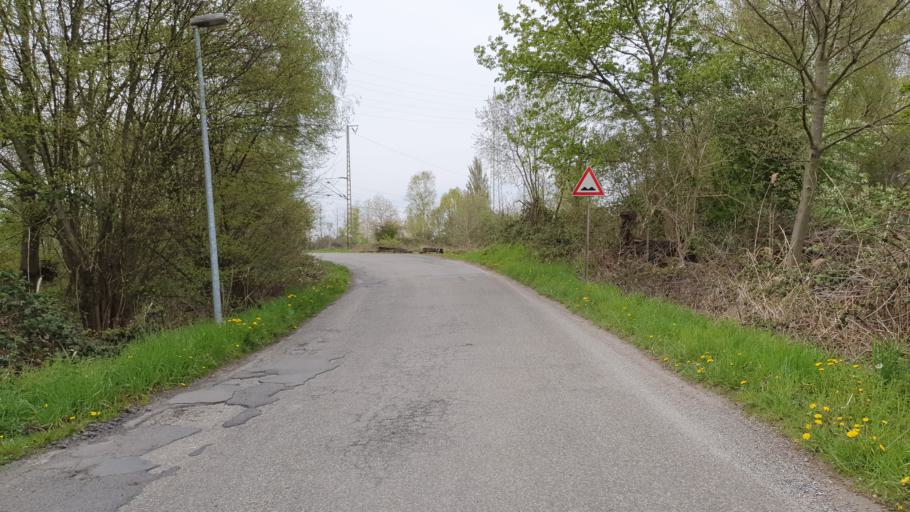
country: DE
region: North Rhine-Westphalia
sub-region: Regierungsbezirk Dusseldorf
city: Oberhausen
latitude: 51.5041
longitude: 6.8470
